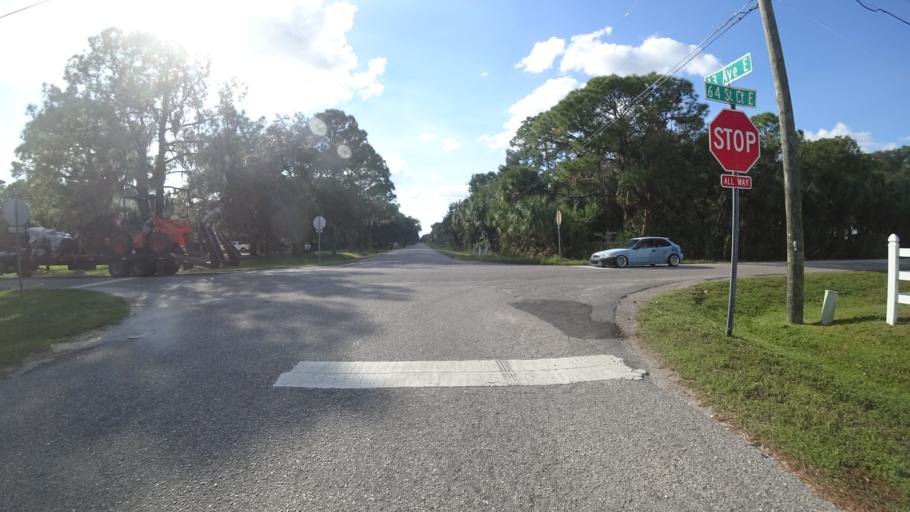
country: US
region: Florida
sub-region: Manatee County
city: Ellenton
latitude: 27.4874
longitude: -82.4792
